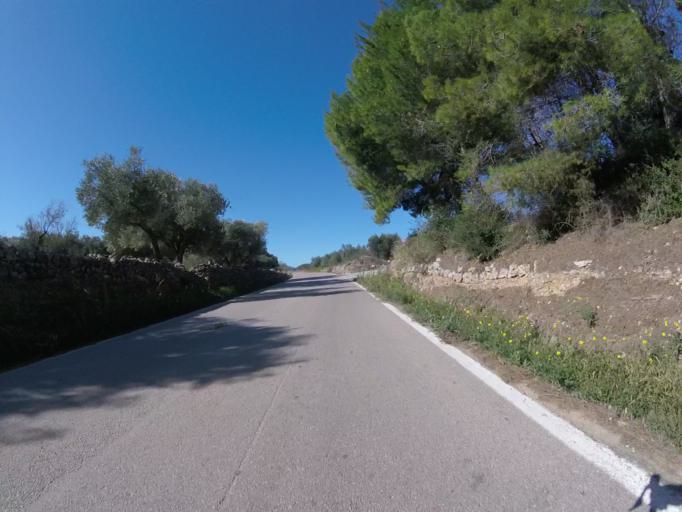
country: ES
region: Valencia
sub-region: Provincia de Castello
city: Chert/Xert
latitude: 40.4644
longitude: 0.1676
